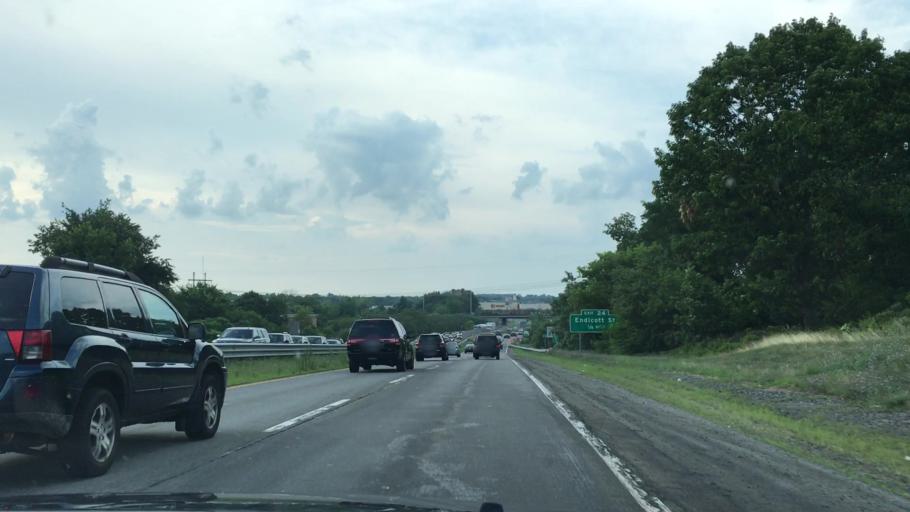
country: US
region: Massachusetts
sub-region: Essex County
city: Peabody
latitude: 42.5452
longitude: -70.9362
